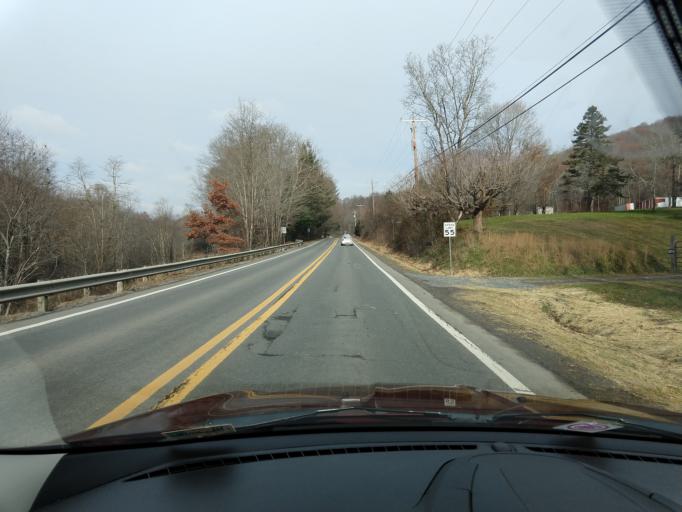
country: US
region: West Virginia
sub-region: Greenbrier County
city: Rainelle
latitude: 37.9656
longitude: -80.6988
